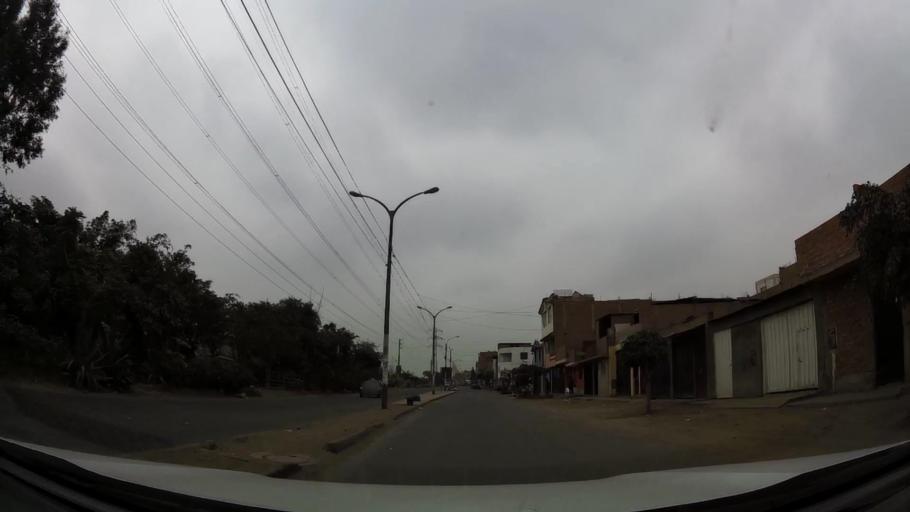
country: PE
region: Lima
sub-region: Lima
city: Independencia
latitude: -11.9439
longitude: -77.0899
